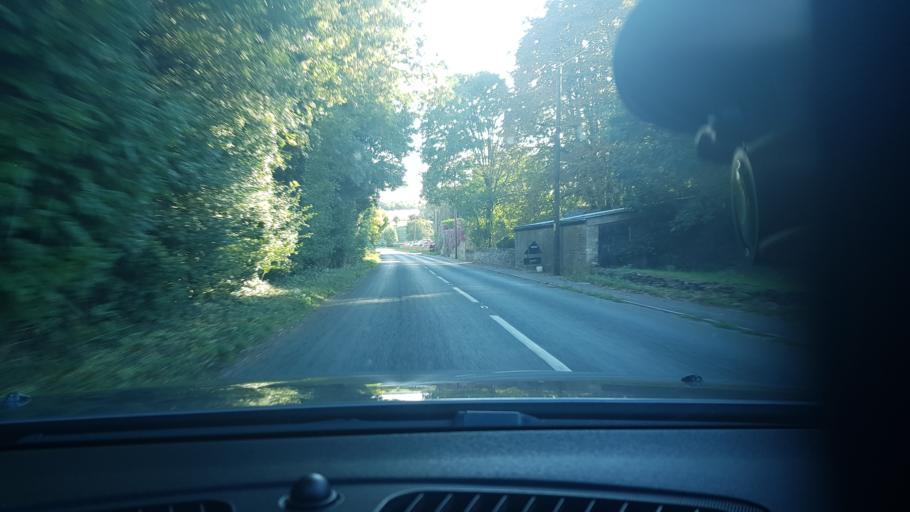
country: GB
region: England
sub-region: Gloucestershire
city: Cirencester
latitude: 51.7446
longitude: -1.9725
